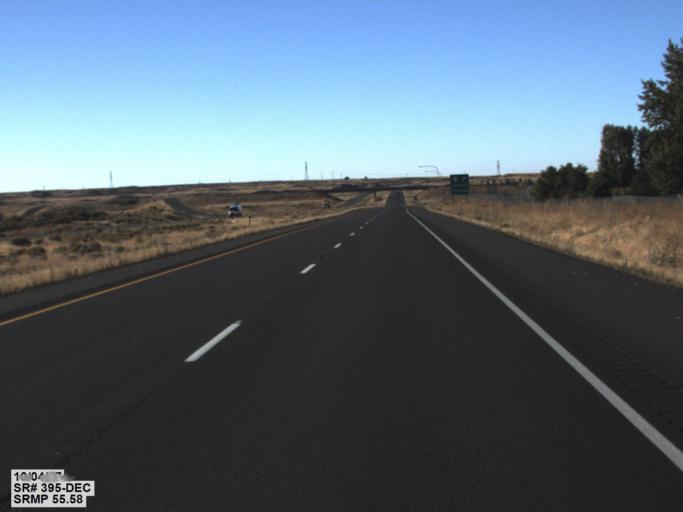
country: US
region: Washington
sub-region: Franklin County
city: Connell
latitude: 46.6584
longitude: -118.8518
